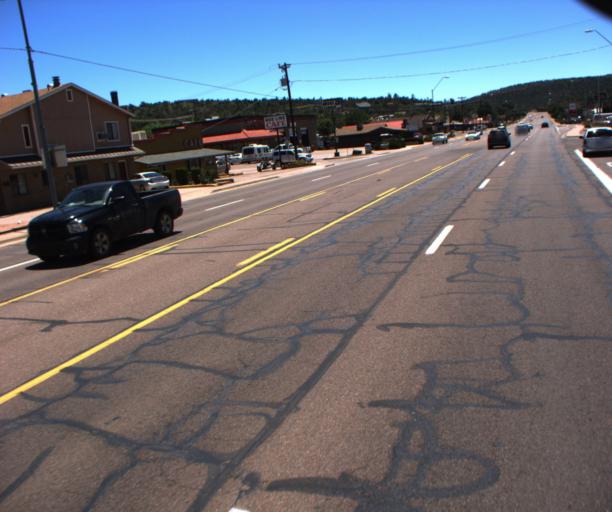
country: US
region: Arizona
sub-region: Gila County
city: Payson
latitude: 34.2301
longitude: -111.3259
